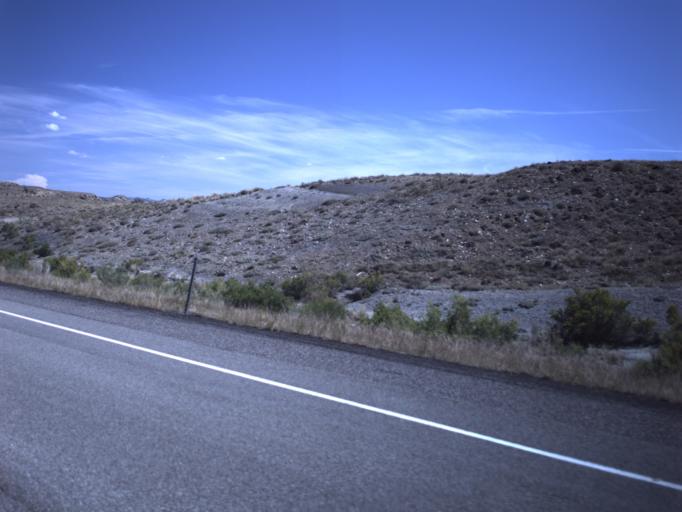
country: US
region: Utah
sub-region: Emery County
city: Ferron
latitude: 38.8116
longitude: -111.2060
